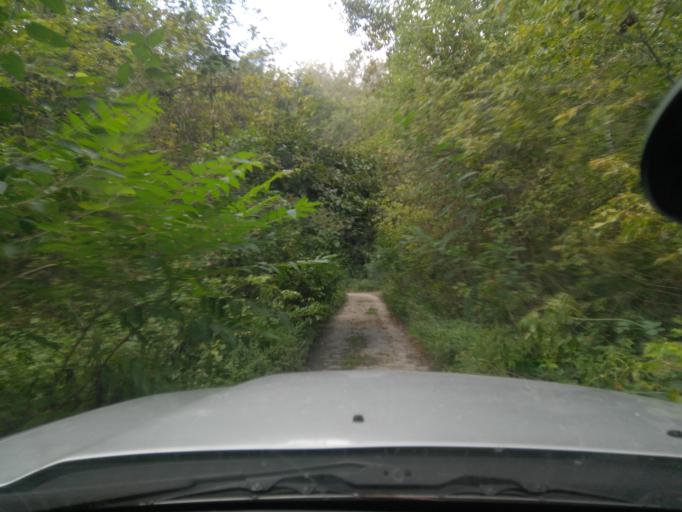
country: HU
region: Bacs-Kiskun
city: Apostag
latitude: 46.8953
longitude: 18.9402
